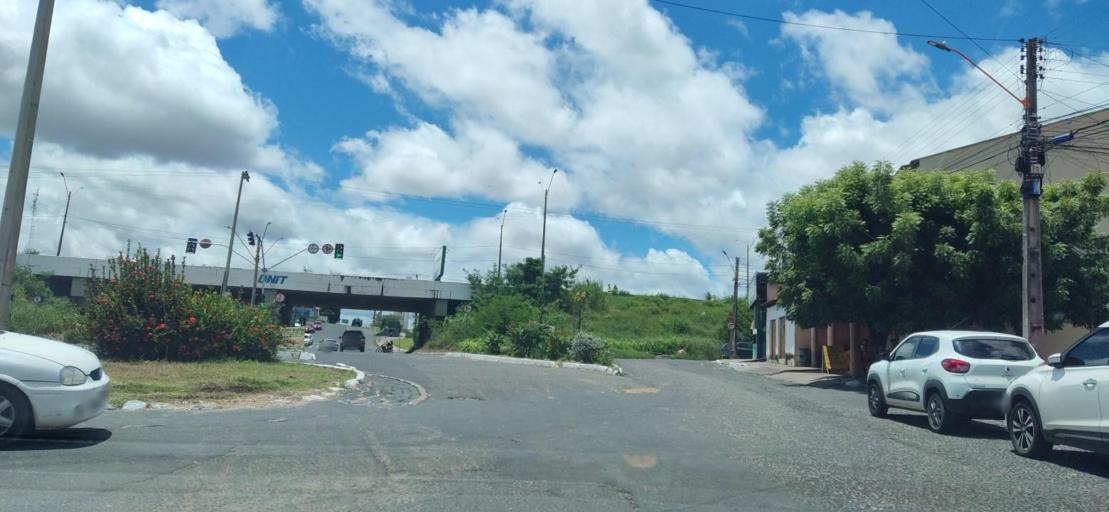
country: BR
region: Piaui
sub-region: Teresina
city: Teresina
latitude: -5.1445
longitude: -42.7784
